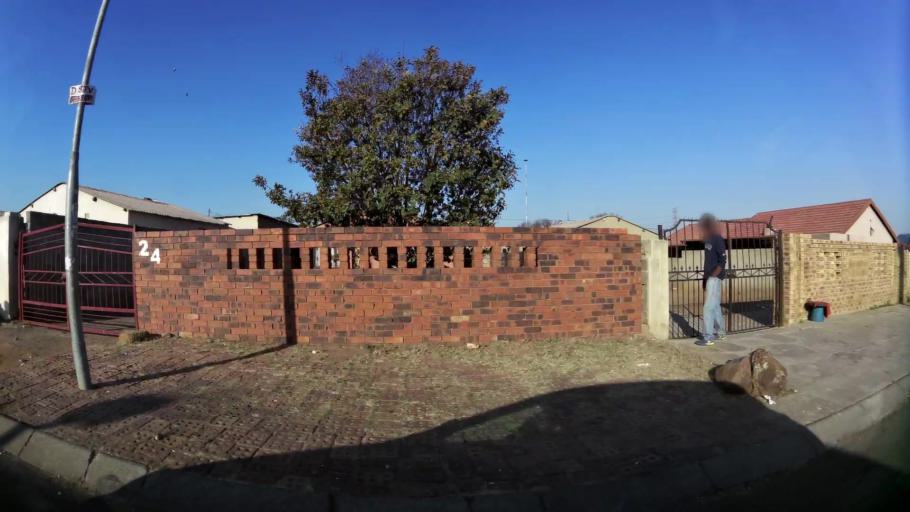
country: ZA
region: Gauteng
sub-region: City of Johannesburg Metropolitan Municipality
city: Soweto
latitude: -26.2610
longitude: 27.8843
